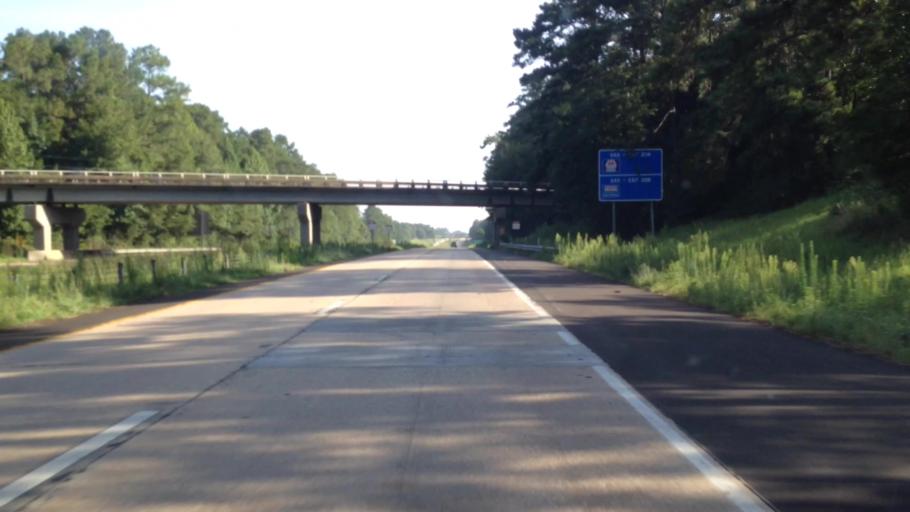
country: US
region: Mississippi
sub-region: Pike County
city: Summit
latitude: 31.2730
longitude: -90.4789
